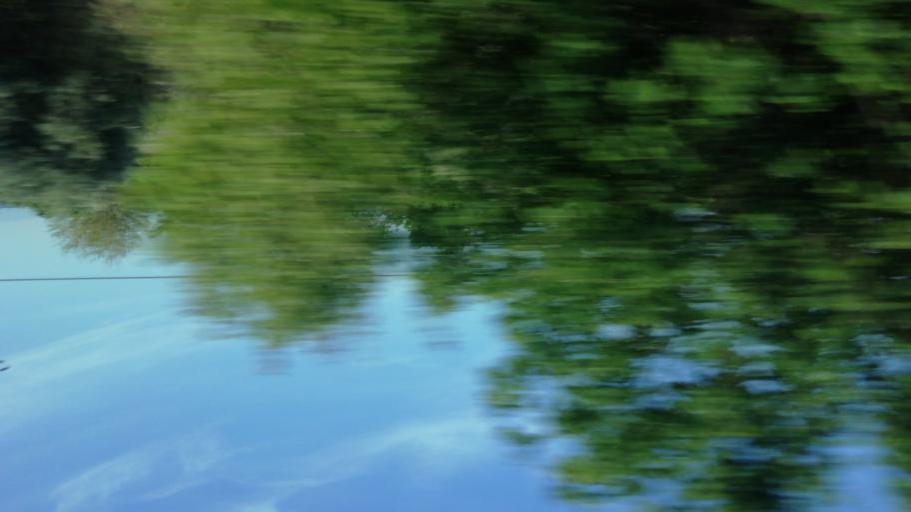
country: TR
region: Manisa
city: Saruhanli
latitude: 38.7360
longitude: 27.5933
